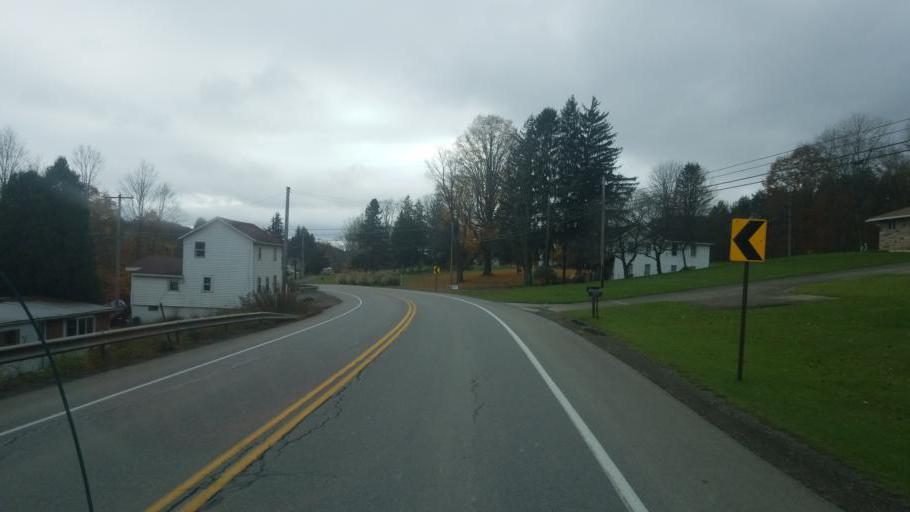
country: US
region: Pennsylvania
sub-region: Jefferson County
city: Brockway
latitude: 41.2666
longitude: -78.7202
